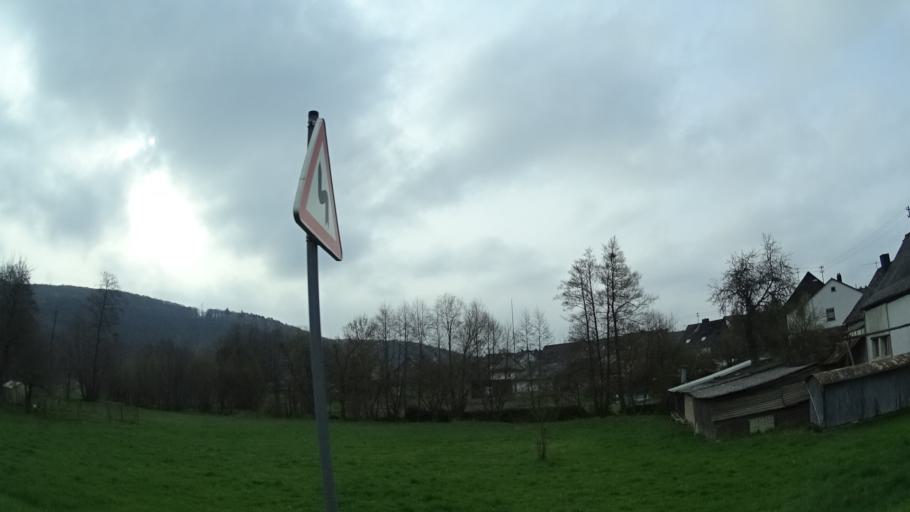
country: DE
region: Rheinland-Pfalz
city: Siesbach
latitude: 49.7323
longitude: 7.2375
